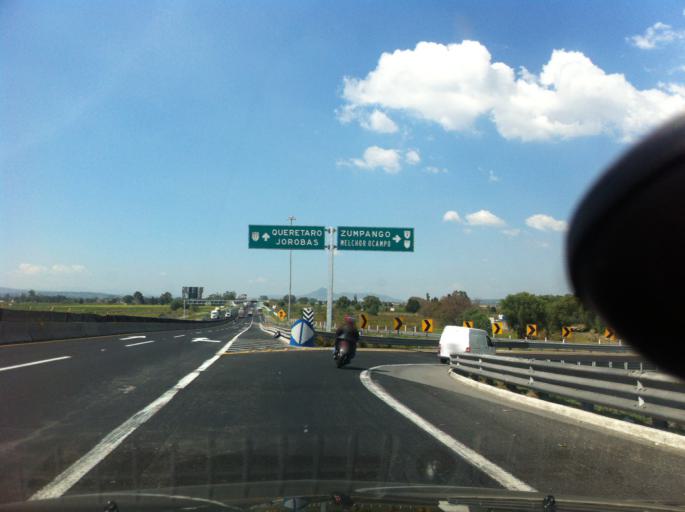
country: MX
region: Mexico
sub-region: Cuautitlan
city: La Providencia
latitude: 19.7527
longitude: -99.1303
